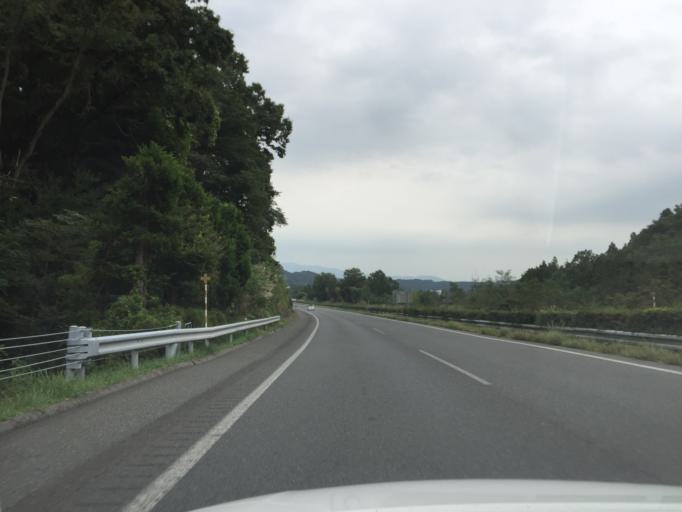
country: JP
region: Fukushima
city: Iwaki
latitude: 37.0577
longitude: 140.8301
